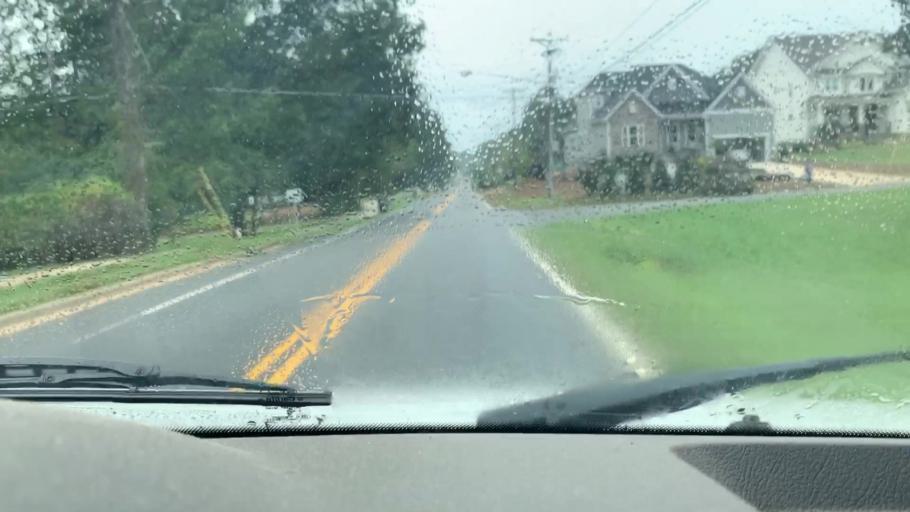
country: US
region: North Carolina
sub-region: Mecklenburg County
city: Cornelius
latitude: 35.4862
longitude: -80.9027
